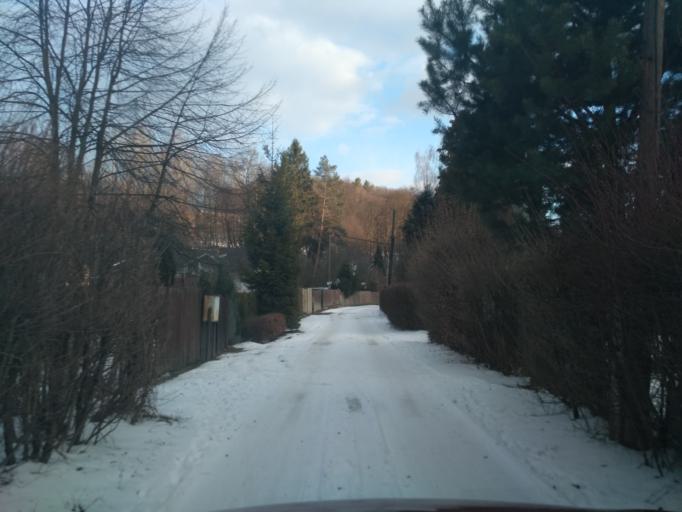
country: SK
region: Kosicky
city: Kosice
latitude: 48.7298
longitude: 21.1620
